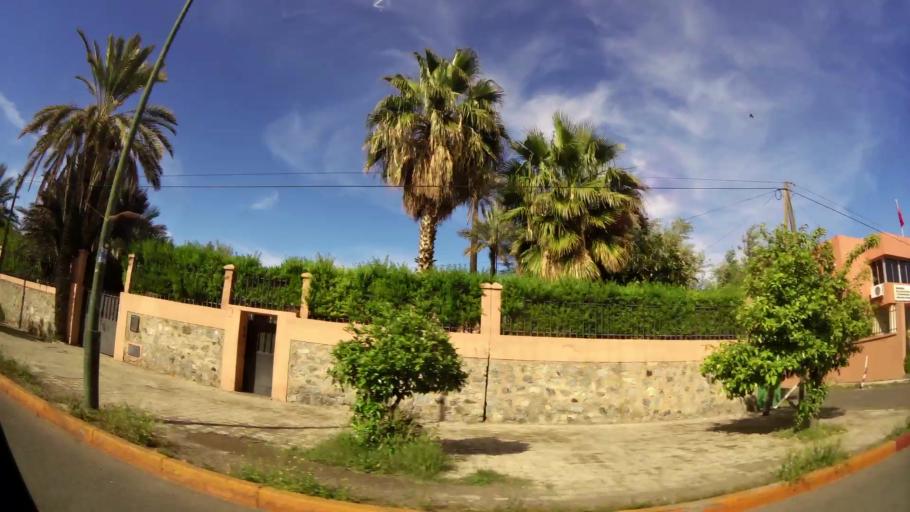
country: MA
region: Marrakech-Tensift-Al Haouz
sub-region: Marrakech
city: Marrakesh
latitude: 31.6509
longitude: -8.0054
